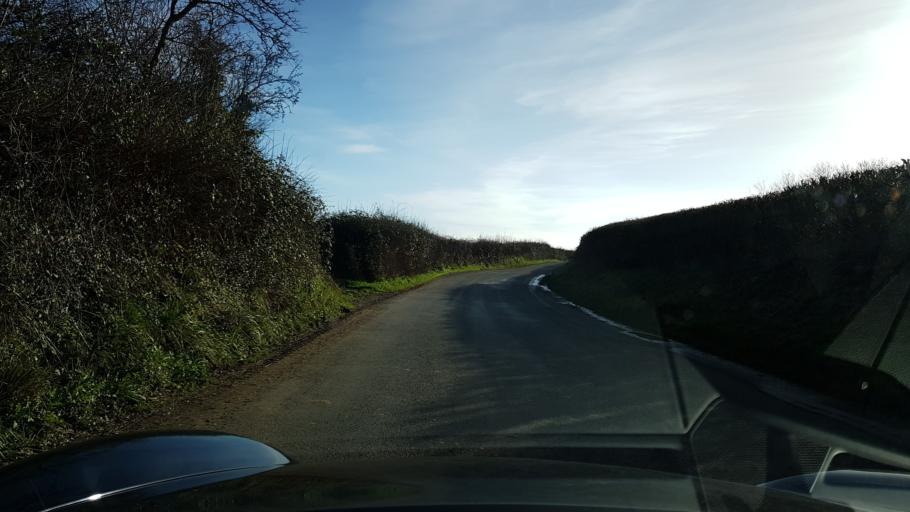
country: GB
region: England
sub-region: Dorset
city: Bridport
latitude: 50.7738
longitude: -2.8107
